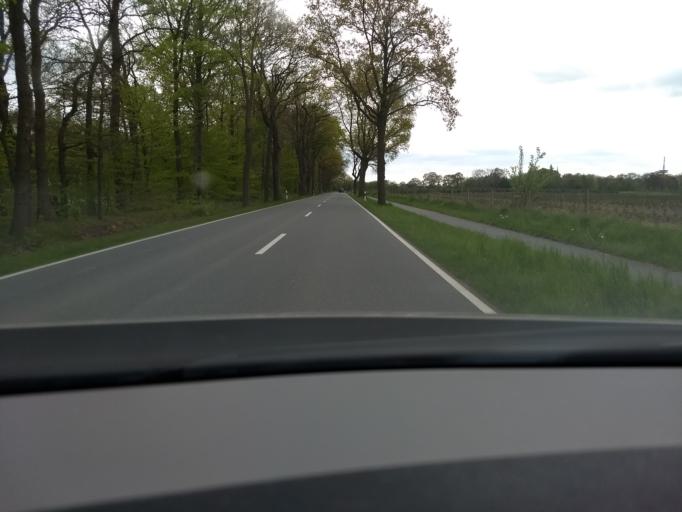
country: DE
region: Lower Saxony
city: Rastede
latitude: 53.2230
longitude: 8.2558
